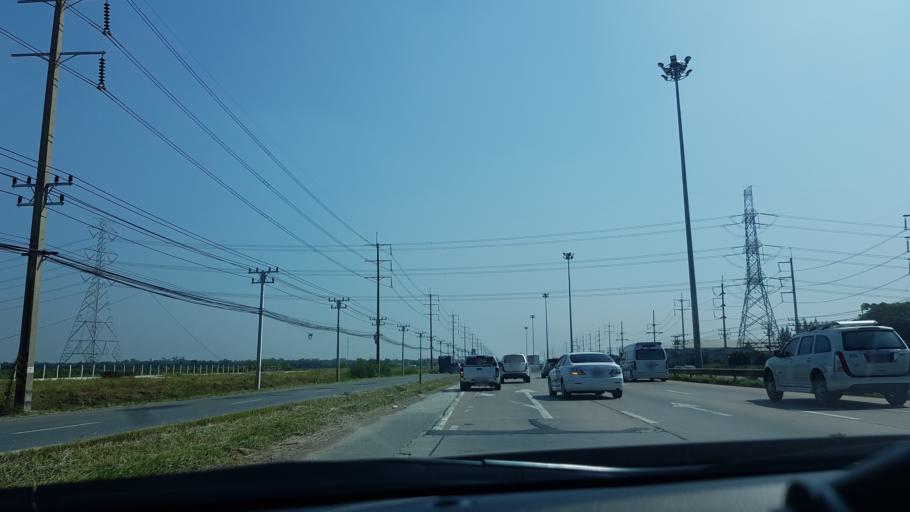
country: TH
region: Phra Nakhon Si Ayutthaya
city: Wang Noi
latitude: 14.2572
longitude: 100.7699
